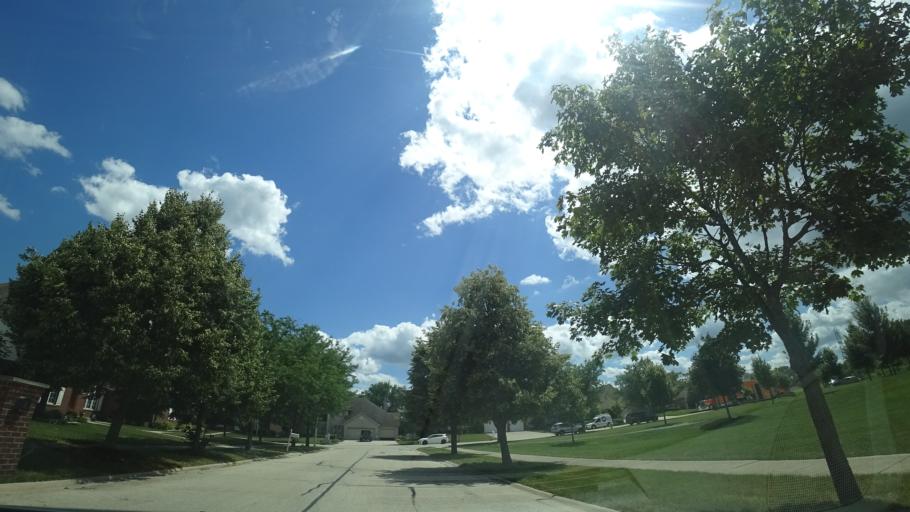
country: US
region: Illinois
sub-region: Will County
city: Homer Glen
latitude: 41.5797
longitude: -87.8963
